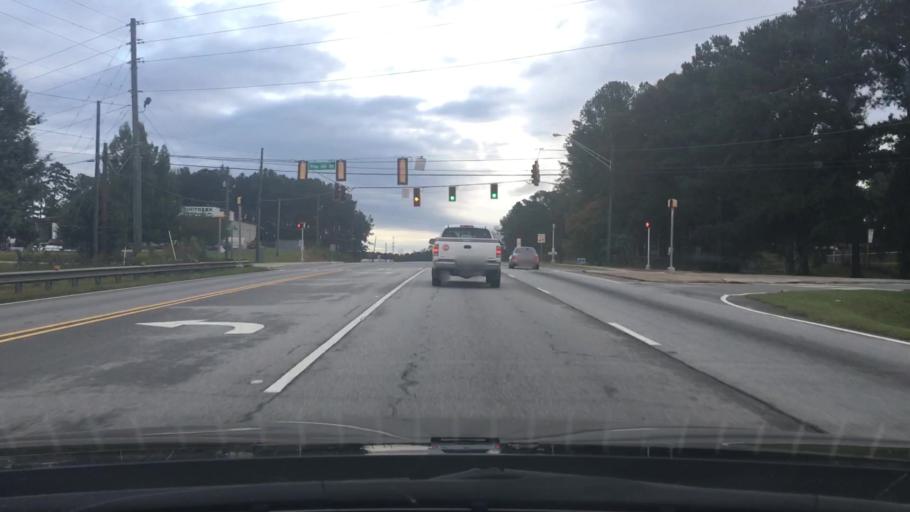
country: US
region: Georgia
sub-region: Spalding County
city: Experiment
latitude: 33.2444
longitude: -84.3081
